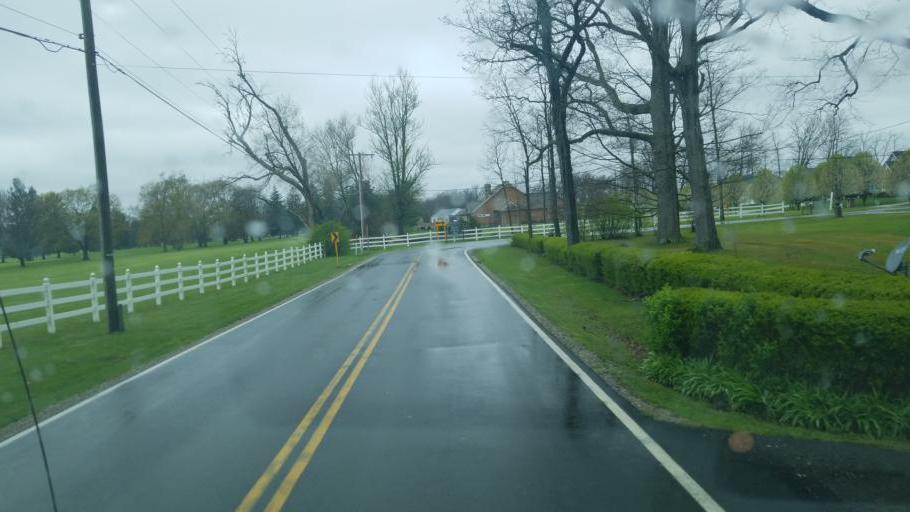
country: US
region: Ohio
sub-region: Marion County
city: Marion
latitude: 40.5421
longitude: -83.1547
